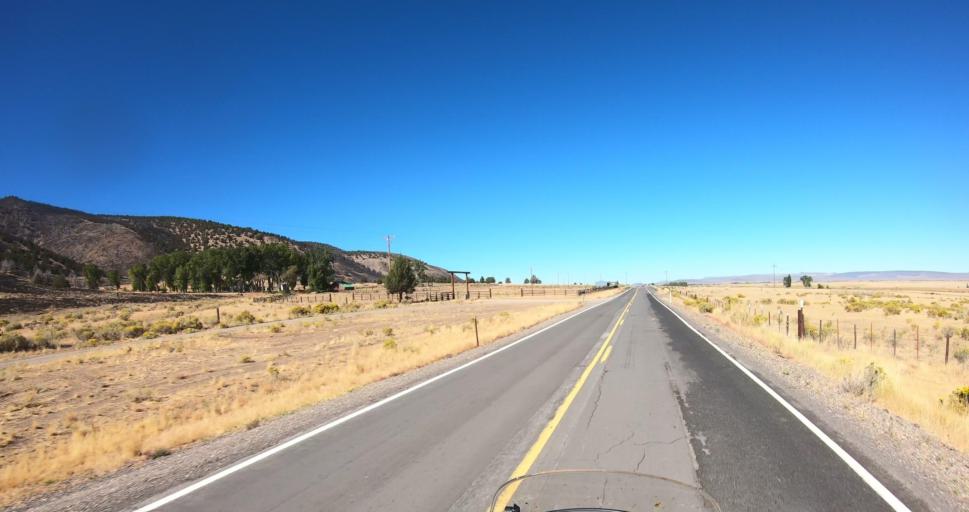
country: US
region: Oregon
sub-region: Lake County
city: Lakeview
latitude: 42.6420
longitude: -120.5200
